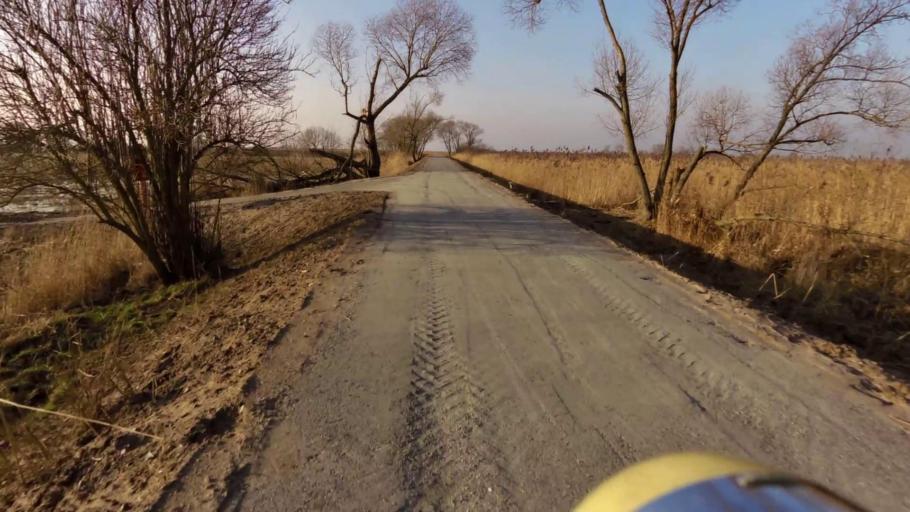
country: PL
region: West Pomeranian Voivodeship
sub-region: Powiat kamienski
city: Wolin
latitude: 53.7561
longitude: 14.5701
